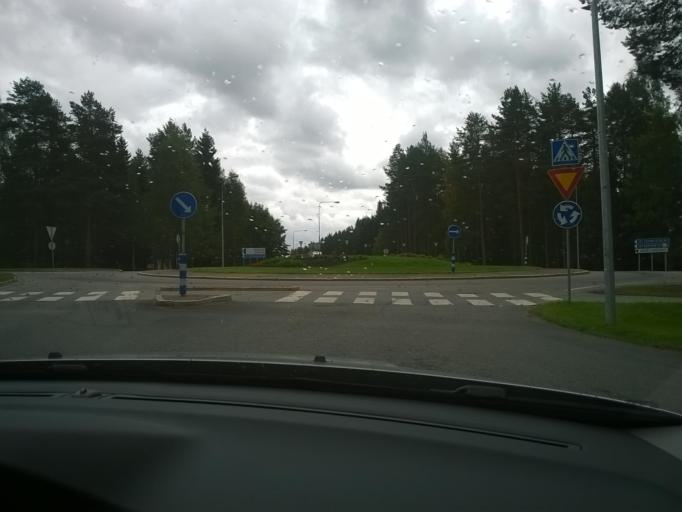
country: FI
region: Kainuu
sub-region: Kehys-Kainuu
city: Kuhmo
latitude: 64.1227
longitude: 29.5076
